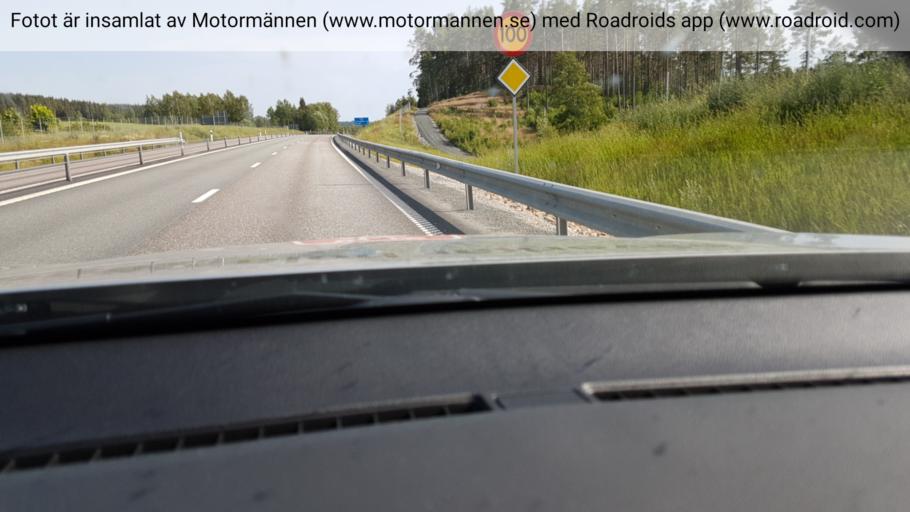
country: SE
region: Joenkoeping
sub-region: Aneby Kommun
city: Aneby
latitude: 57.8126
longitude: 14.8617
